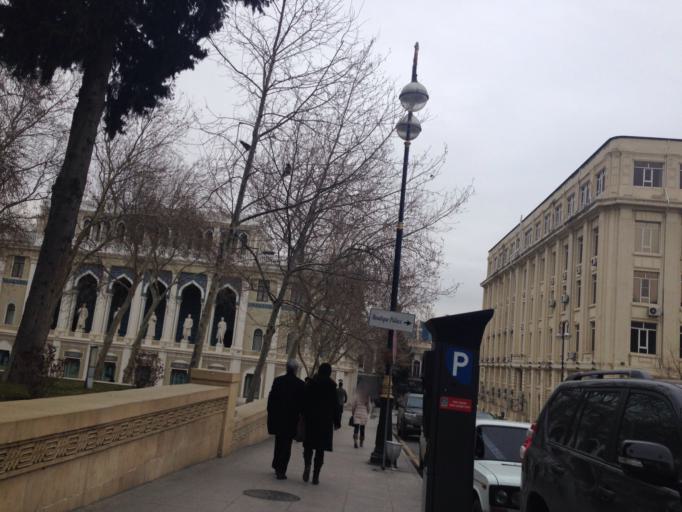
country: AZ
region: Baki
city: Badamdar
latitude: 40.3694
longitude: 49.8357
